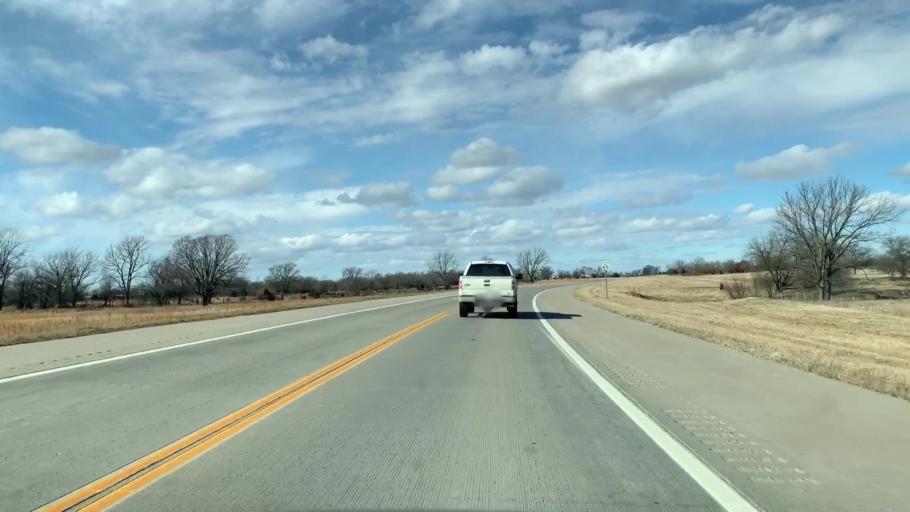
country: US
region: Kansas
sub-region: Labette County
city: Parsons
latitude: 37.3433
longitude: -95.1829
